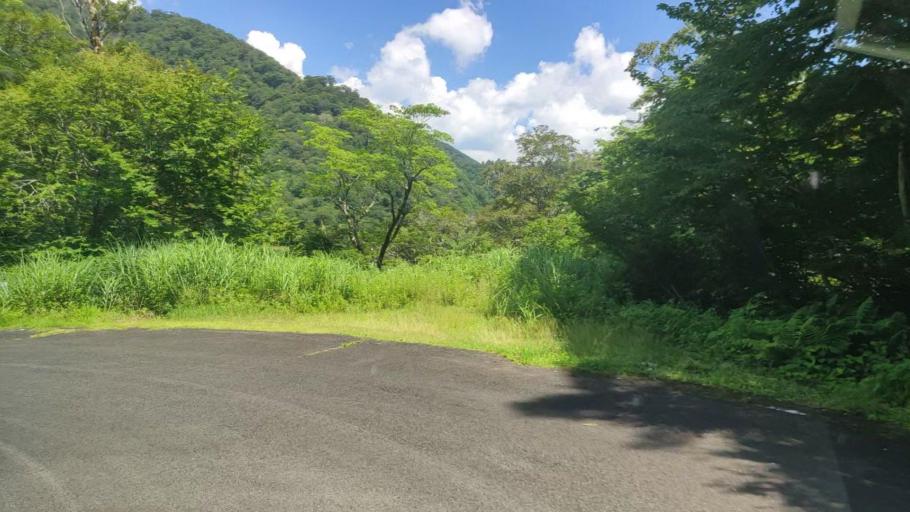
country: JP
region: Fukui
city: Ono
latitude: 35.7748
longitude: 136.5249
